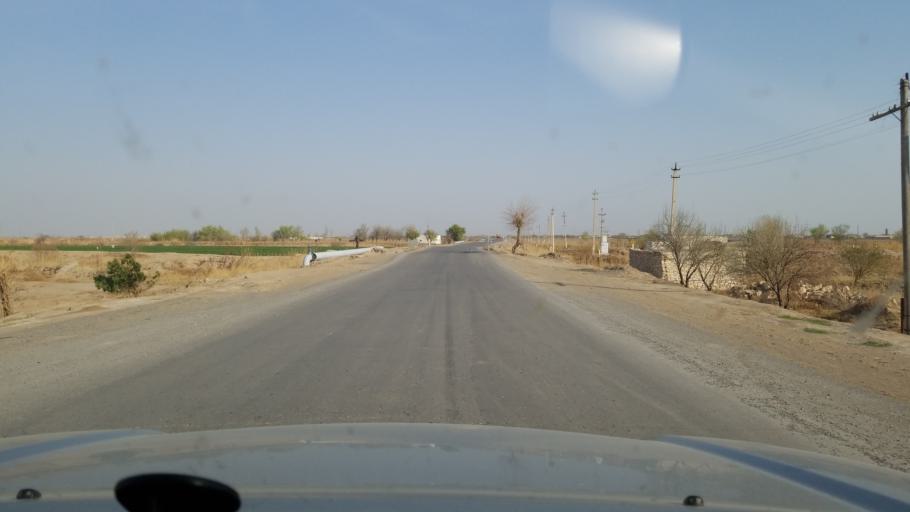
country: AF
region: Jowzjan
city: Khamyab
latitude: 37.6095
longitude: 65.7286
